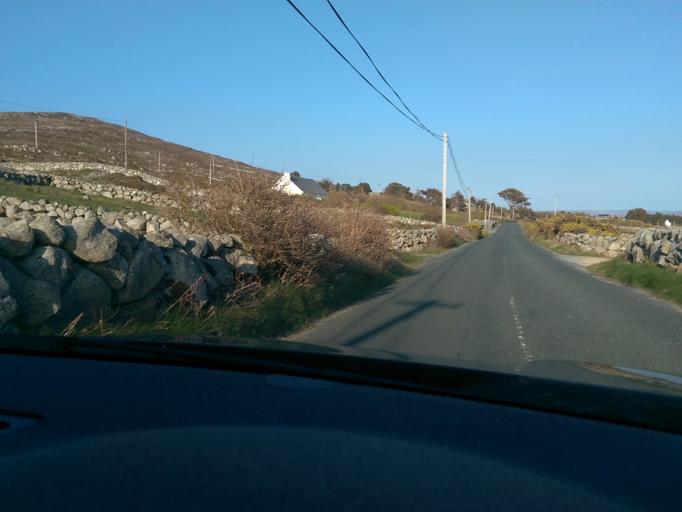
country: IE
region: Connaught
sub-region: County Galway
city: Clifden
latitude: 53.3090
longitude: -9.7576
